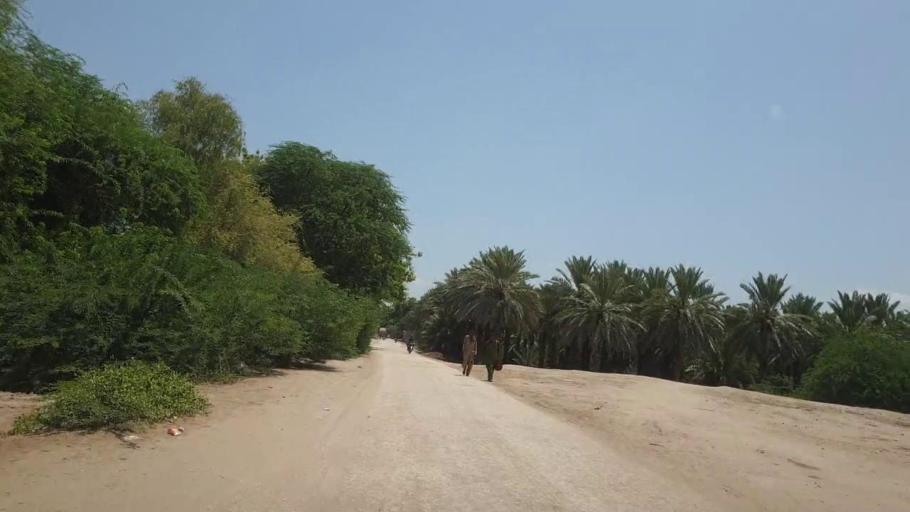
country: PK
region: Sindh
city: Pano Aqil
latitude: 27.6621
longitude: 69.1660
